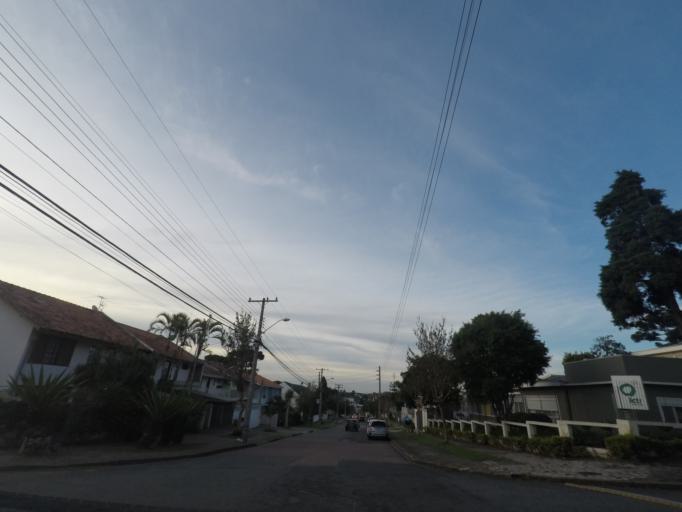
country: BR
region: Parana
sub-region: Curitiba
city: Curitiba
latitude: -25.4199
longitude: -49.2843
